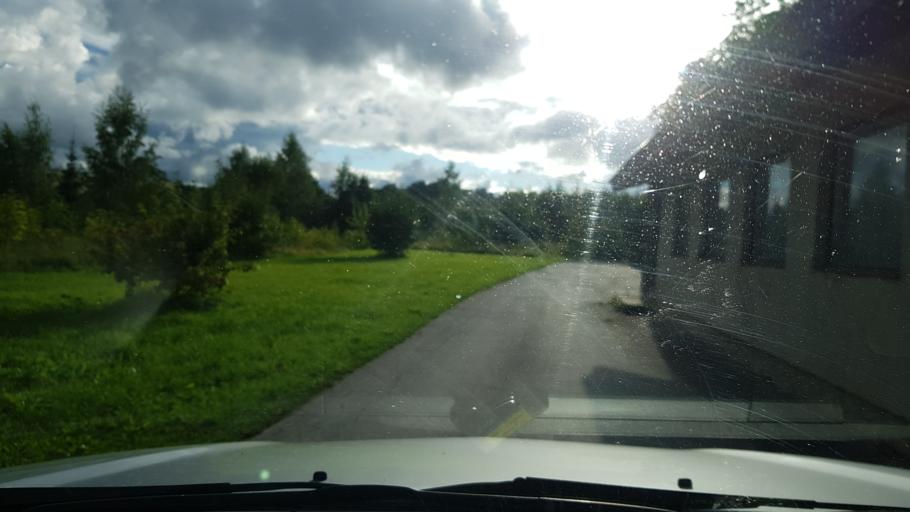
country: EE
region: Harju
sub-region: Rae vald
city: Jueri
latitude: 59.3609
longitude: 24.9202
